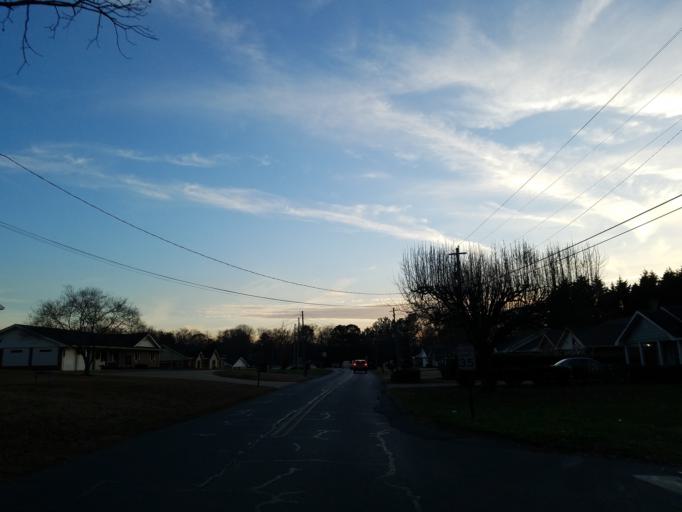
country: US
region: Georgia
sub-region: Bartow County
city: Cartersville
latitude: 34.1891
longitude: -84.8165
